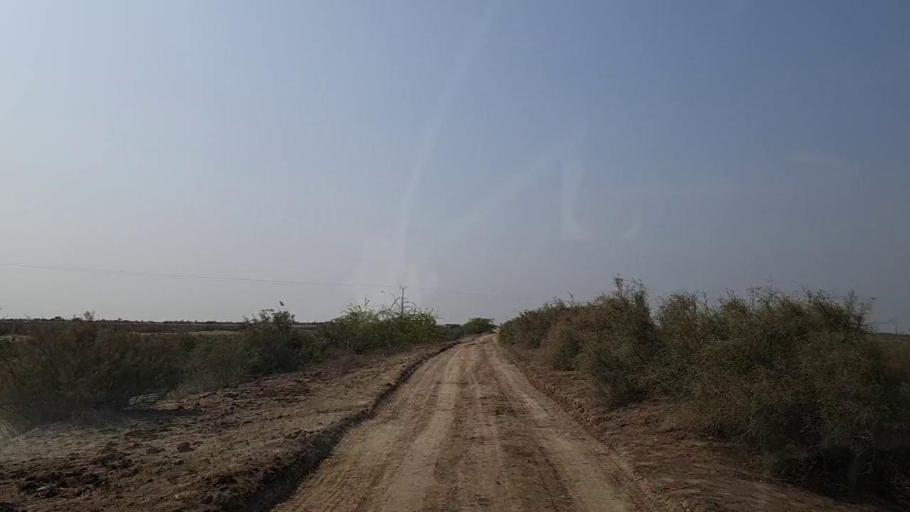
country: PK
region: Sindh
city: Gharo
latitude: 24.6735
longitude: 67.7035
